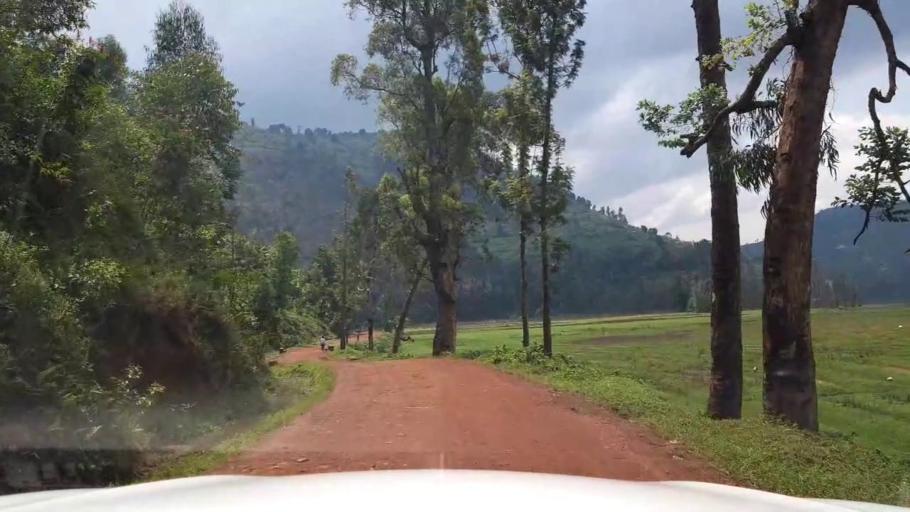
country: UG
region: Western Region
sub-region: Kisoro District
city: Kisoro
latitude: -1.3818
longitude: 29.7960
